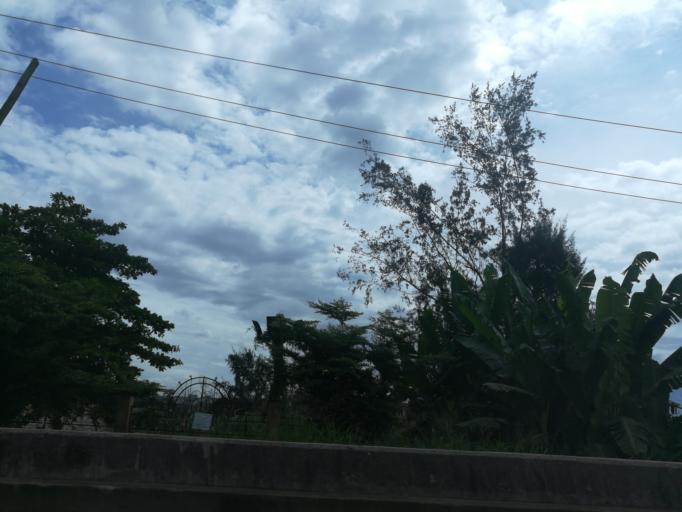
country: NG
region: Lagos
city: Somolu
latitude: 6.5550
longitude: 3.3722
